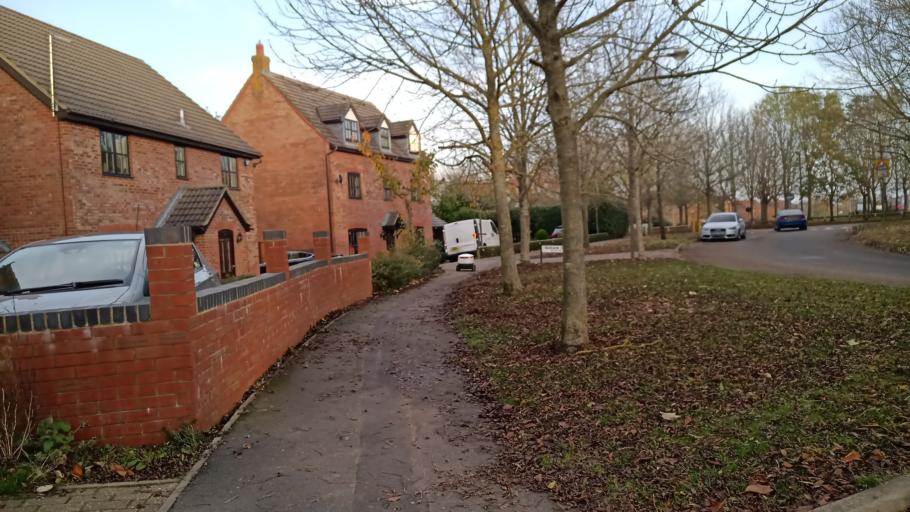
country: GB
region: England
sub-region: Milton Keynes
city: Shenley Church End
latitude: 52.0085
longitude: -0.7883
